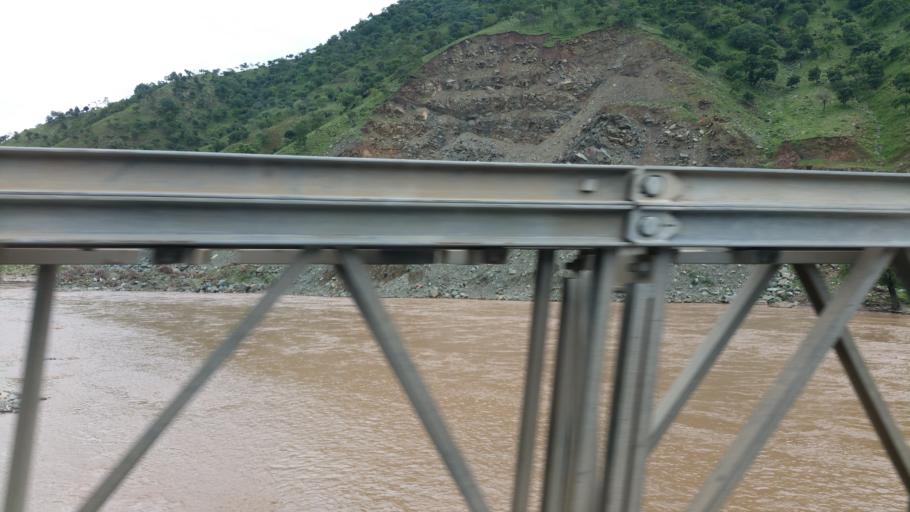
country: ET
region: Tigray
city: Inda Silase
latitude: 13.7367
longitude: 38.1979
